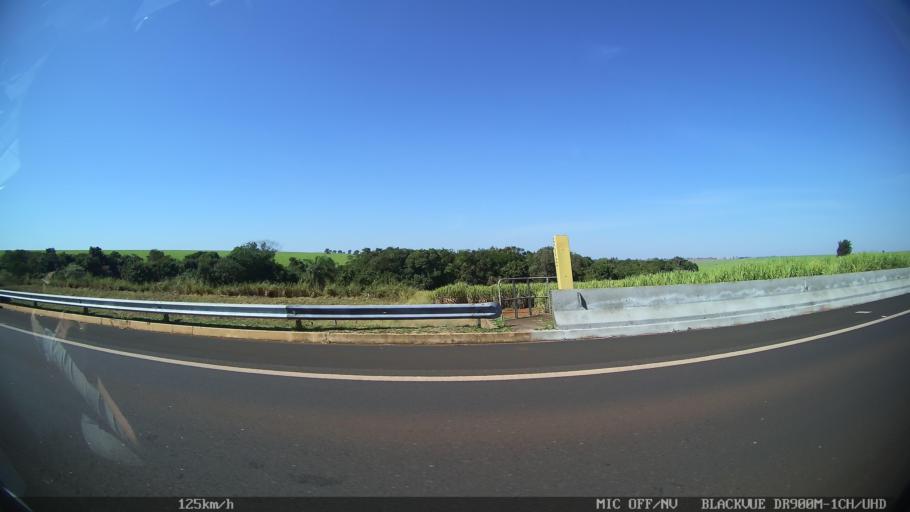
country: BR
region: Sao Paulo
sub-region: Batatais
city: Batatais
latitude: -20.8240
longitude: -47.5921
